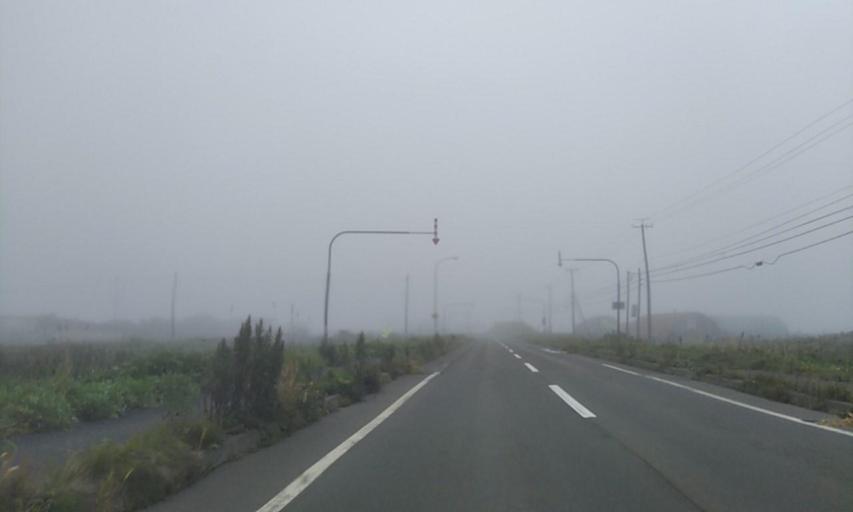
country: JP
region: Hokkaido
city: Nemuro
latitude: 43.3727
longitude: 145.8034
